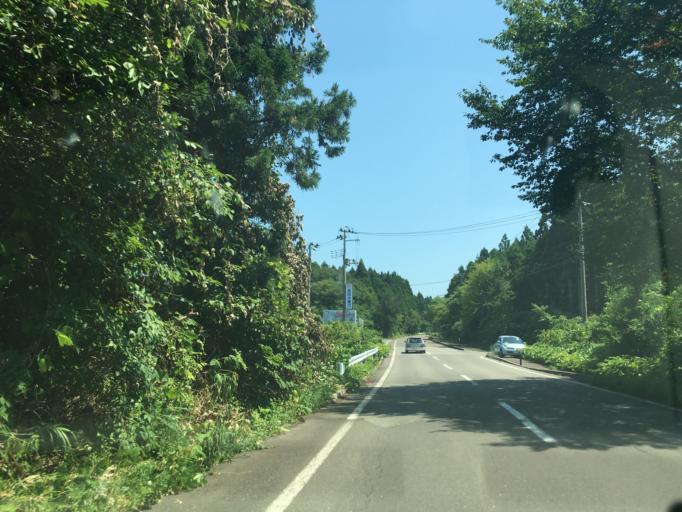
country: JP
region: Akita
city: Tenno
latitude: 39.9812
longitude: 139.7233
